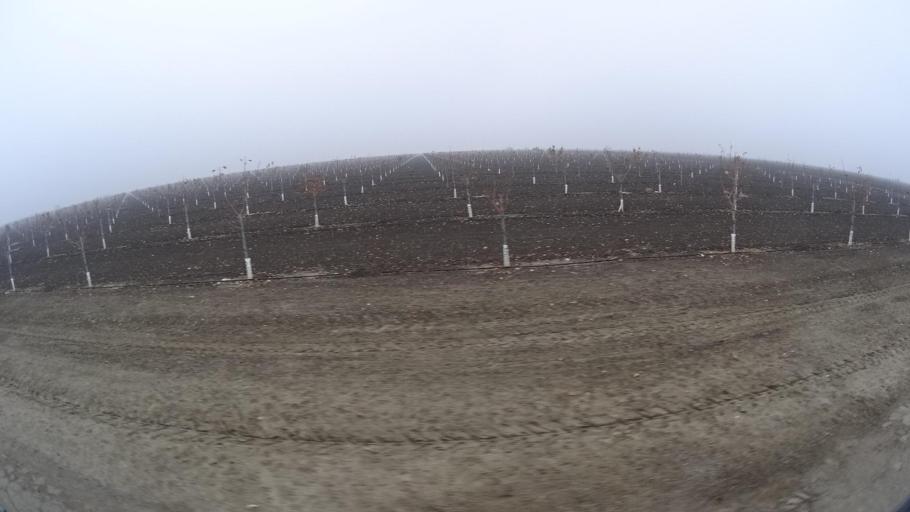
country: US
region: California
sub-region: Kern County
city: Buttonwillow
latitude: 35.4497
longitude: -119.5176
